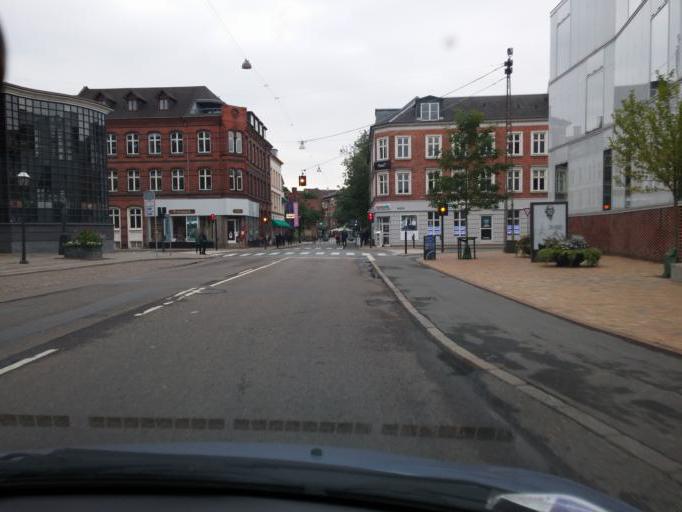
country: DK
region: South Denmark
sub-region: Odense Kommune
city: Odense
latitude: 55.3986
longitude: 10.3848
